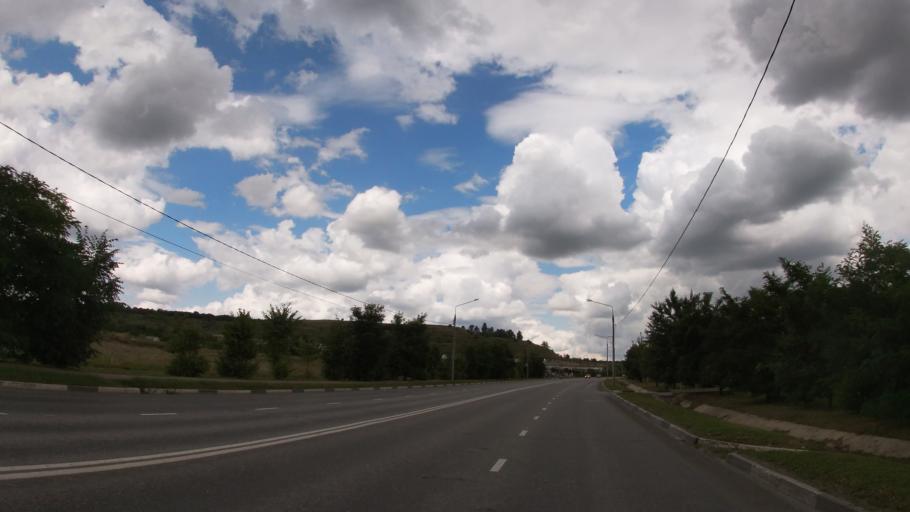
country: RU
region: Belgorod
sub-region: Belgorodskiy Rayon
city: Belgorod
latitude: 50.6133
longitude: 36.6130
